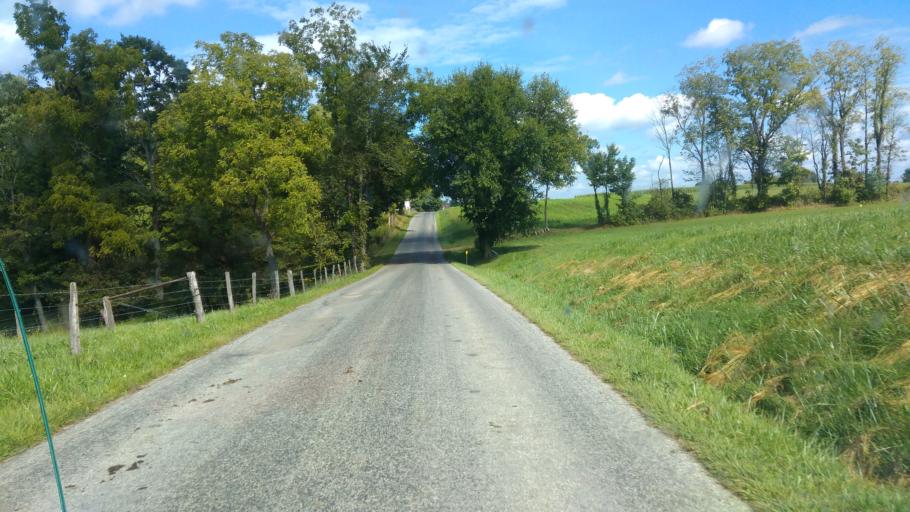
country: US
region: Ohio
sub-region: Holmes County
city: Millersburg
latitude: 40.6198
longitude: -81.8370
